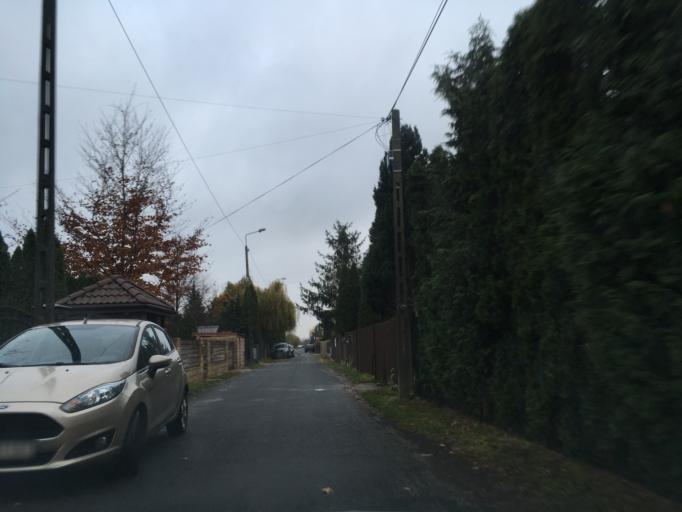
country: PL
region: Masovian Voivodeship
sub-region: Powiat pruszkowski
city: Brwinow
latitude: 52.1405
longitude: 20.7360
